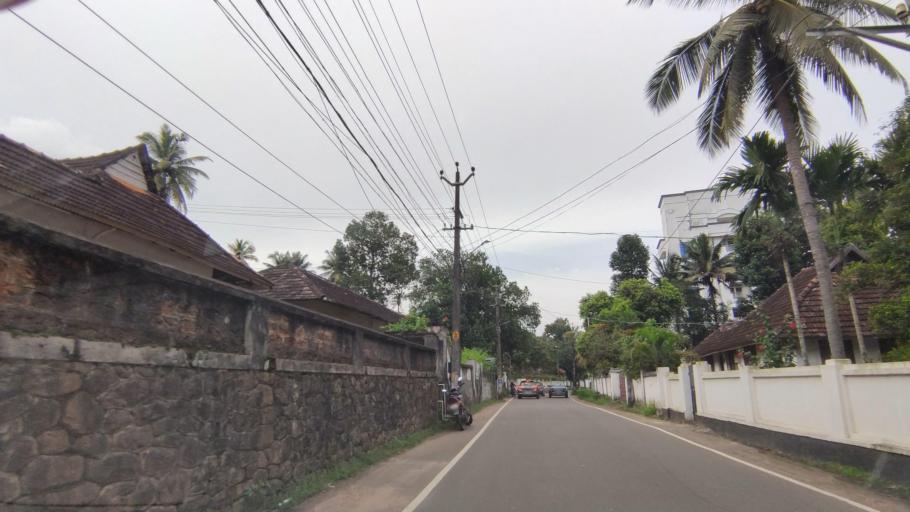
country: IN
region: Kerala
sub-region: Kottayam
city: Kottayam
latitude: 9.5922
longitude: 76.5116
